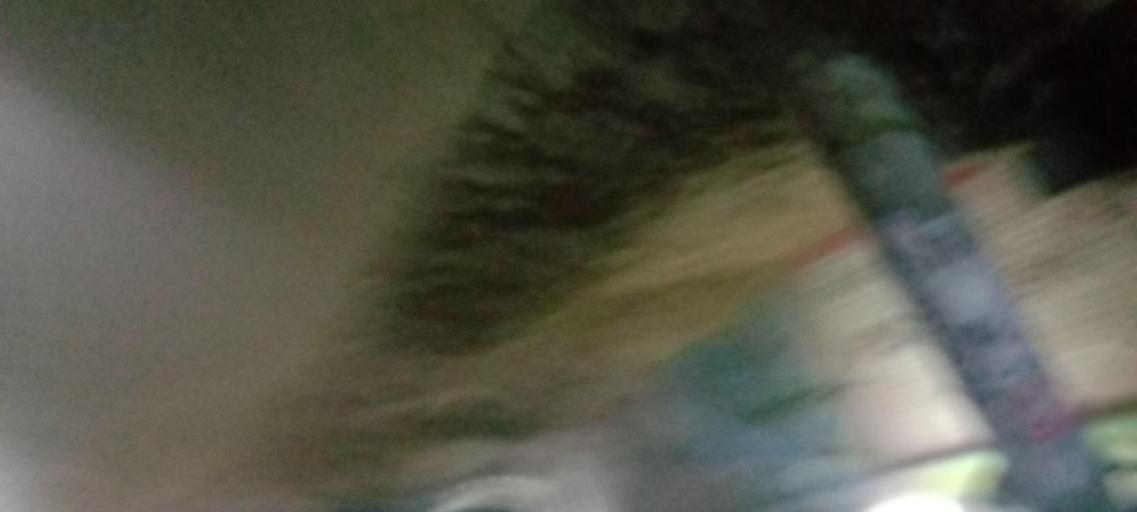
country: BD
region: Dhaka
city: Azimpur
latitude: 23.7001
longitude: 90.3681
